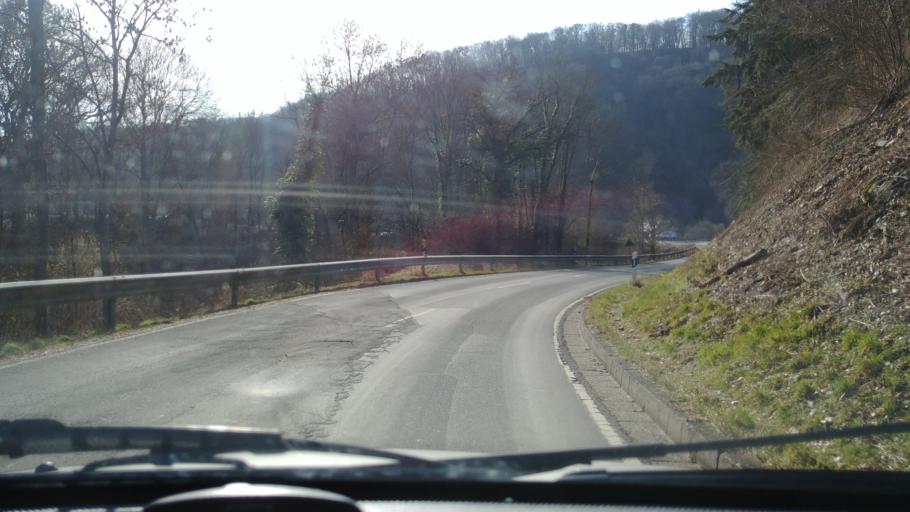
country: DE
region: Rheinland-Pfalz
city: Montenich
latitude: 50.2380
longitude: 7.2918
